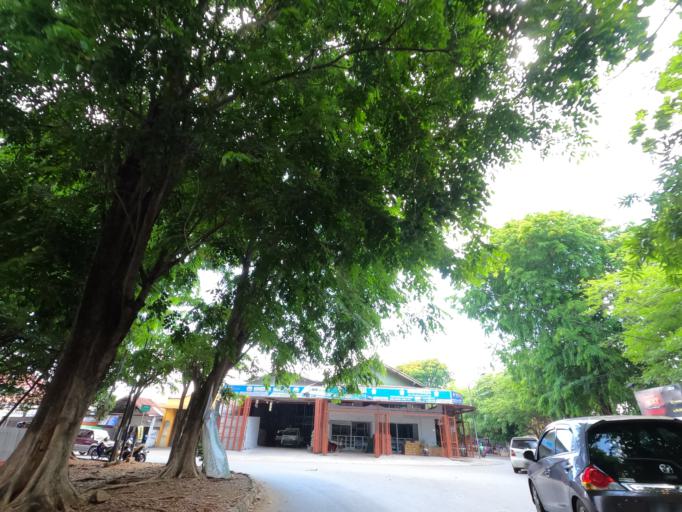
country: ID
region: West Java
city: Pamanukan
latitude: -6.5582
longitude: 107.7603
